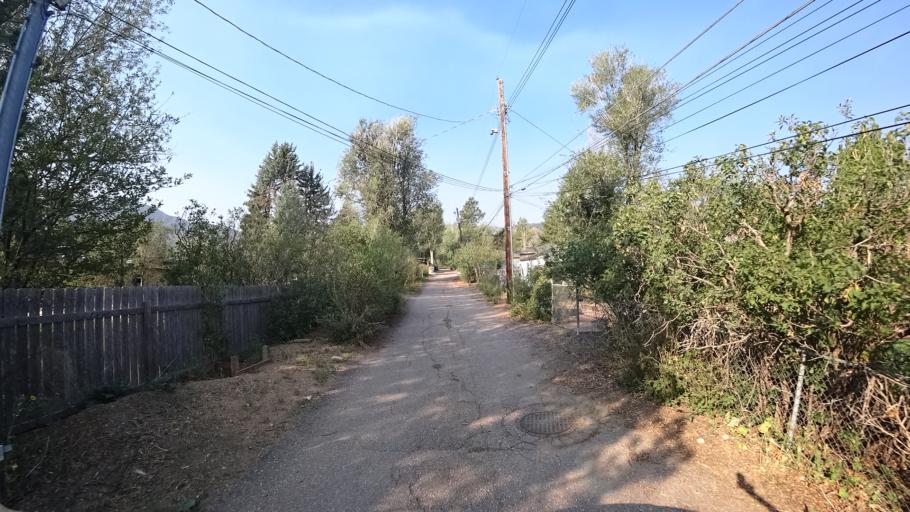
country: US
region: Colorado
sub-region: El Paso County
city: Colorado Springs
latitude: 38.8010
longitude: -104.8545
